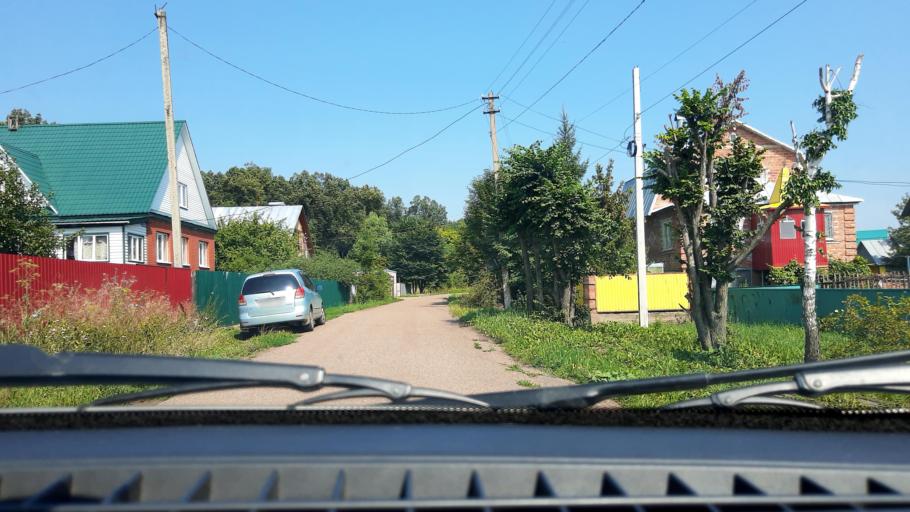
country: RU
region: Bashkortostan
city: Mikhaylovka
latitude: 54.8403
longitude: 55.8272
